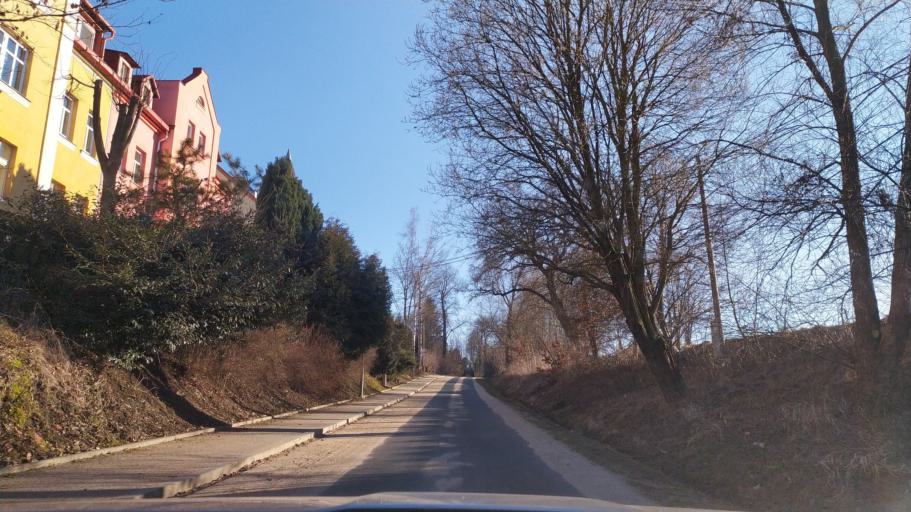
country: CZ
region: Karlovarsky
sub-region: Okres Cheb
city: Frantiskovy Lazne
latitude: 50.1120
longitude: 12.3498
